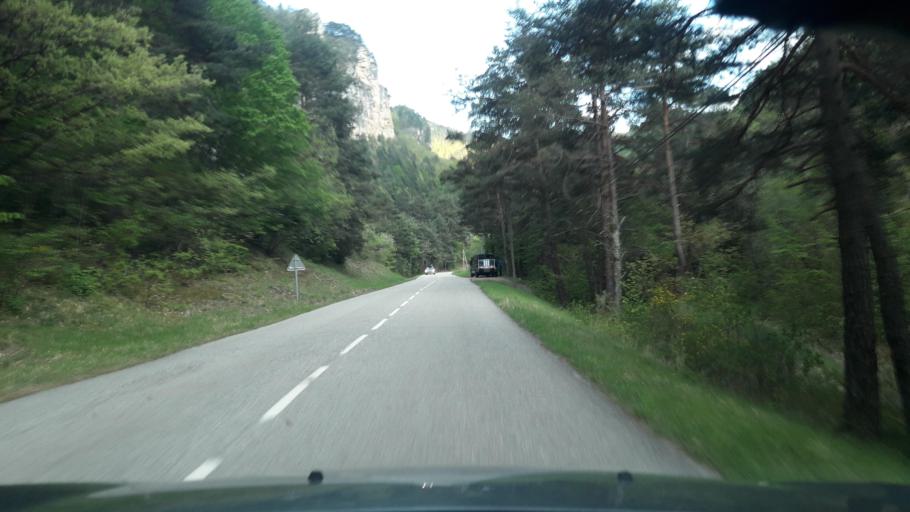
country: FR
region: Rhone-Alpes
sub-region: Departement de la Drome
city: Die
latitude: 44.6723
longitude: 5.5366
